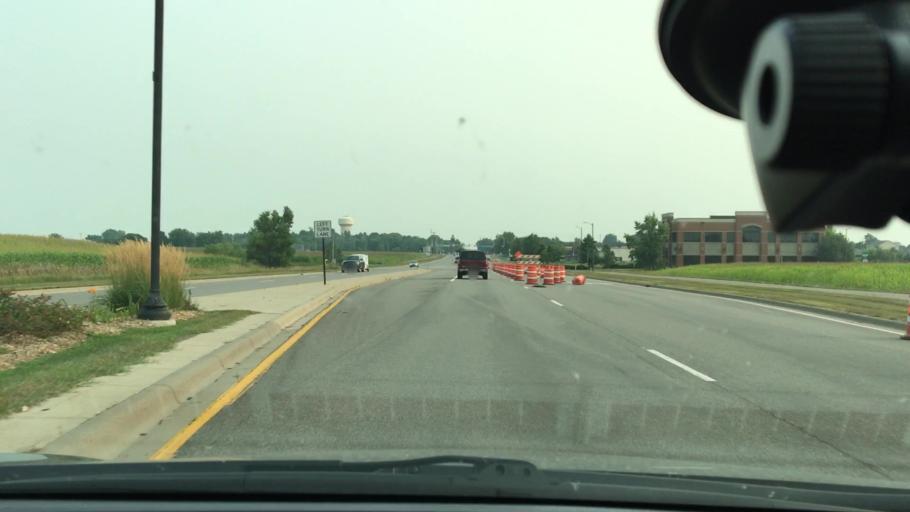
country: US
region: Minnesota
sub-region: Wright County
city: Albertville
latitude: 45.2300
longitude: -93.6644
